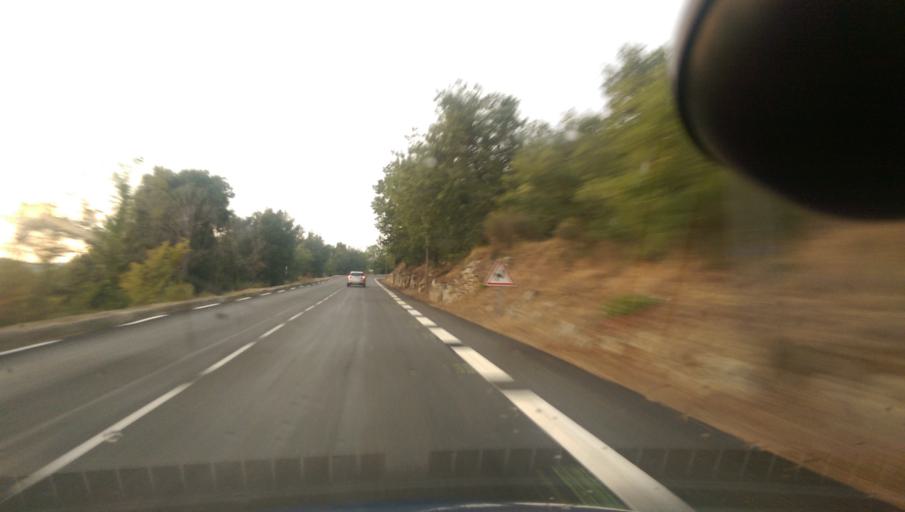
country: FR
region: Provence-Alpes-Cote d'Azur
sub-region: Departement des Alpes-Maritimes
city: Grasse
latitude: 43.6683
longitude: 6.9144
